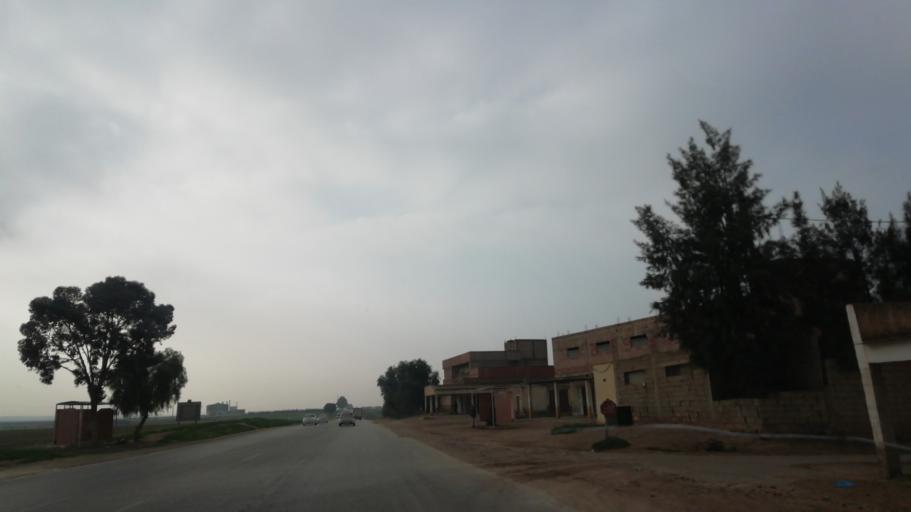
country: DZ
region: Relizane
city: Djidiouia
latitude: 35.8840
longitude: 0.7328
